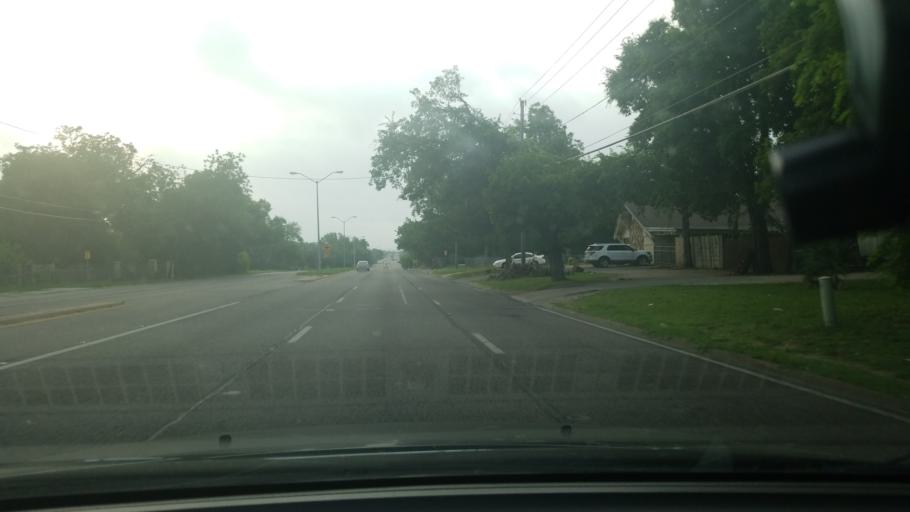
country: US
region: Texas
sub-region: Dallas County
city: Balch Springs
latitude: 32.7634
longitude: -96.6753
